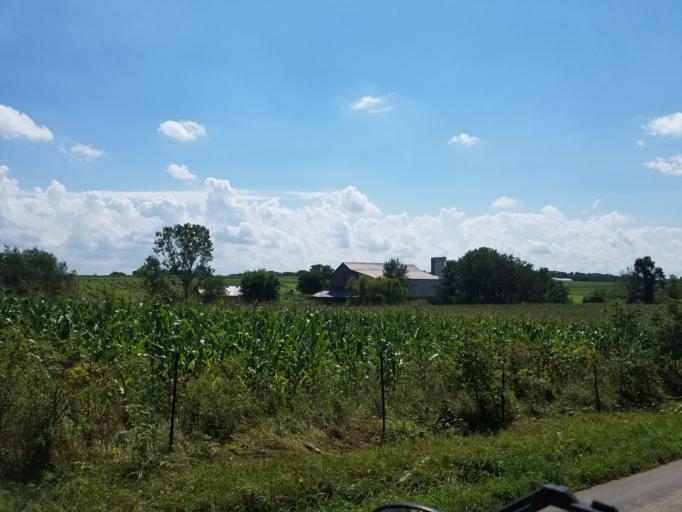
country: US
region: Ohio
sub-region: Knox County
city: Fredericktown
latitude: 40.5251
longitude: -82.6137
